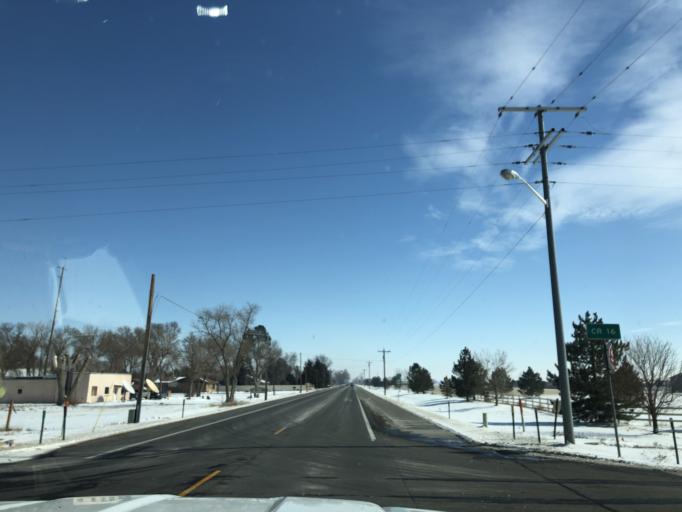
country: US
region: Colorado
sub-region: Morgan County
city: Fort Morgan
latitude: 40.2540
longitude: -103.8491
